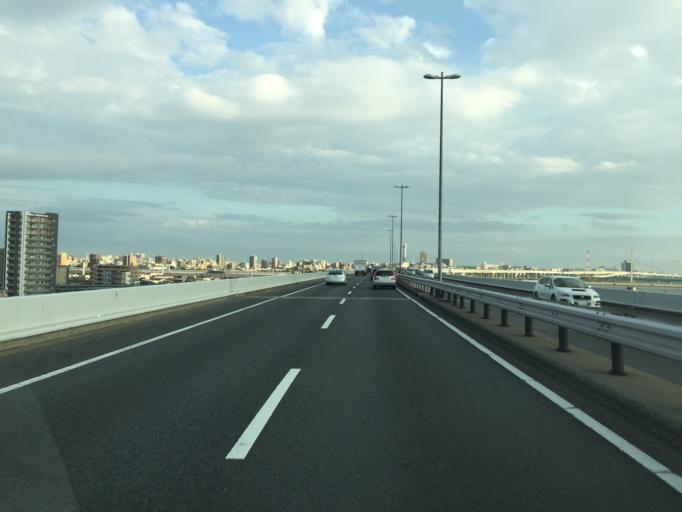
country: JP
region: Tokyo
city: Urayasu
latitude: 35.7044
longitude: 139.8585
